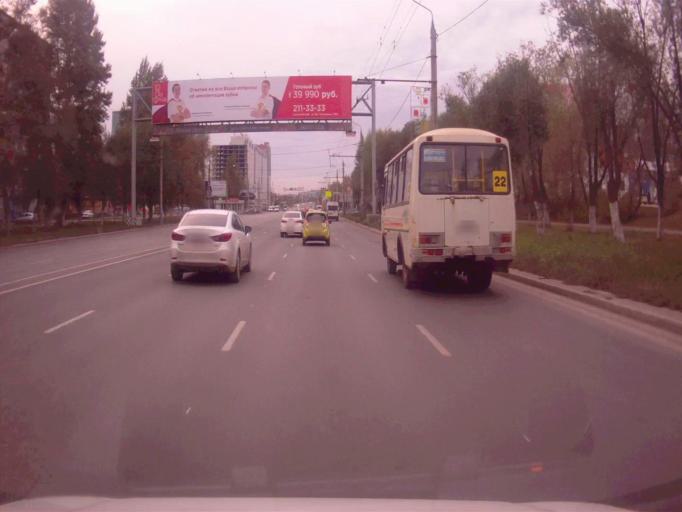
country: RU
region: Chelyabinsk
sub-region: Gorod Chelyabinsk
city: Chelyabinsk
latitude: 55.1787
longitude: 61.3378
